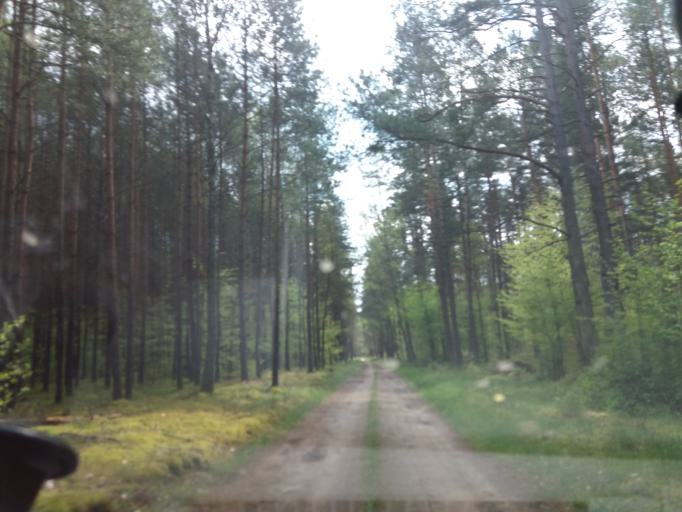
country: PL
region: West Pomeranian Voivodeship
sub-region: Powiat choszczenski
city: Drawno
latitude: 53.1249
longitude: 15.8508
